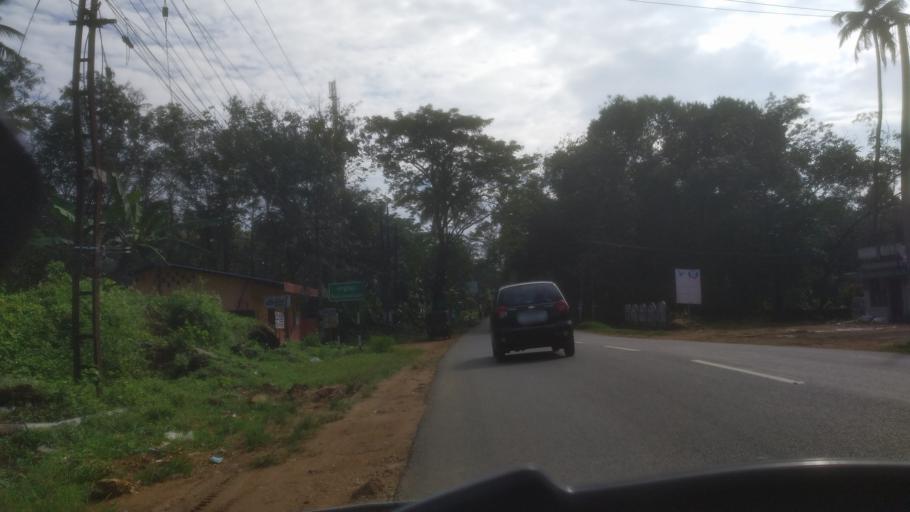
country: IN
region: Kerala
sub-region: Ernakulam
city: Kotamangalam
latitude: 10.0587
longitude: 76.6789
